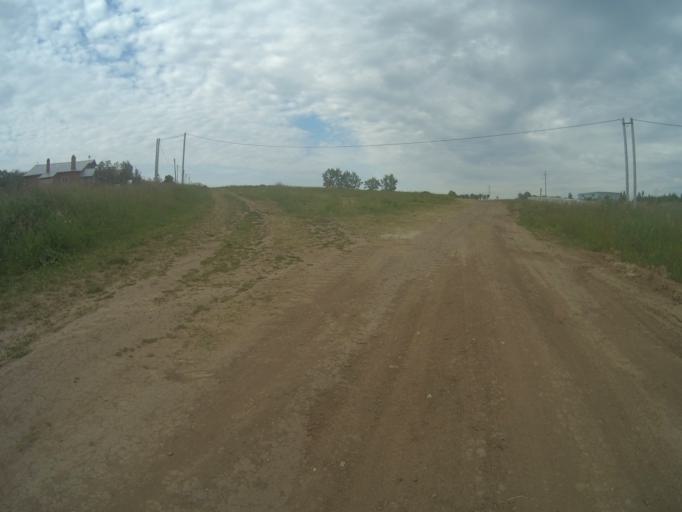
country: RU
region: Vladimir
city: Bogolyubovo
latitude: 56.1872
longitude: 40.5047
